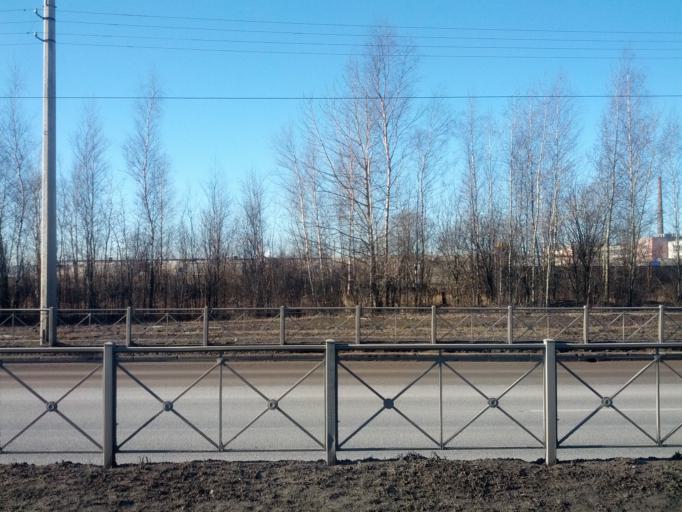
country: RU
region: St.-Petersburg
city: Obukhovo
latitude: 59.9048
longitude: 30.4544
